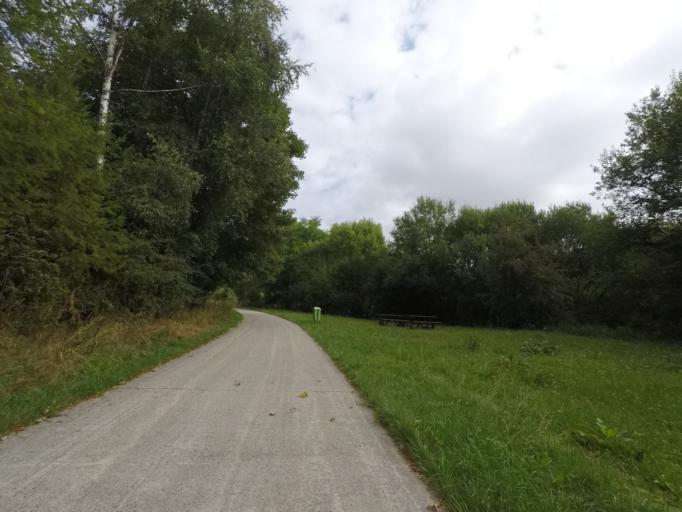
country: BE
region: Wallonia
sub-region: Province du Luxembourg
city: Martelange
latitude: 49.8231
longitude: 5.7530
